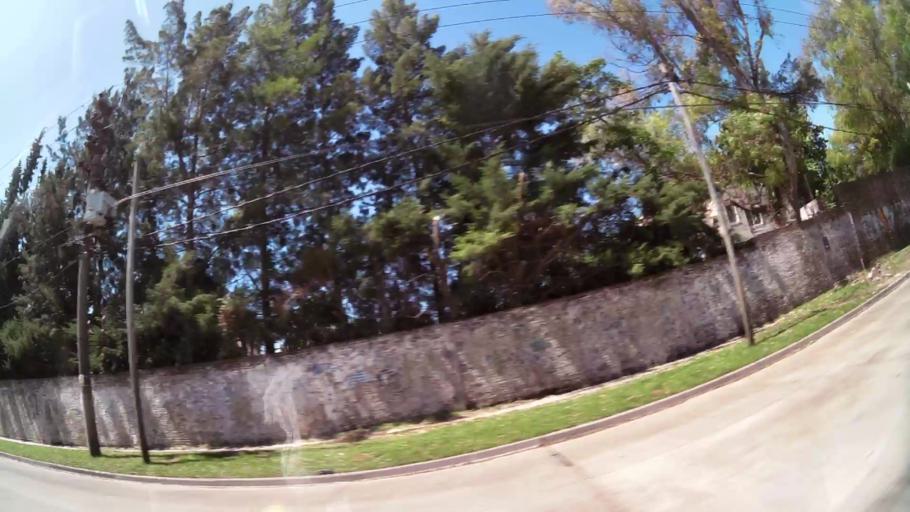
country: AR
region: Buenos Aires
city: Hurlingham
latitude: -34.4975
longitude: -58.6512
